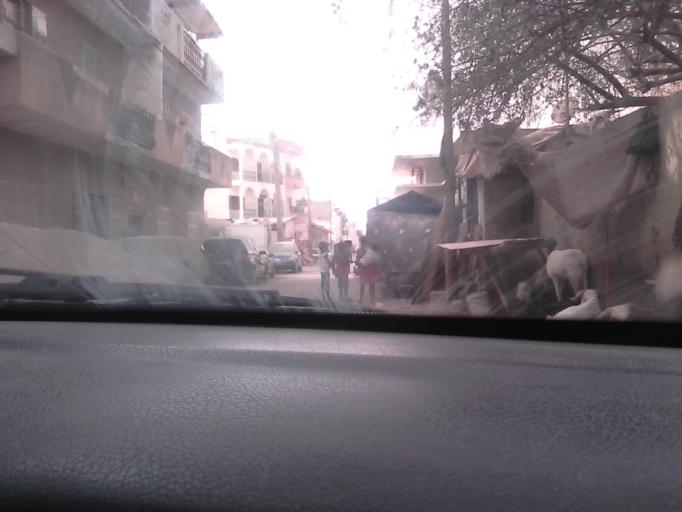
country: SN
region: Dakar
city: Grand Dakar
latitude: 14.7042
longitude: -17.4530
